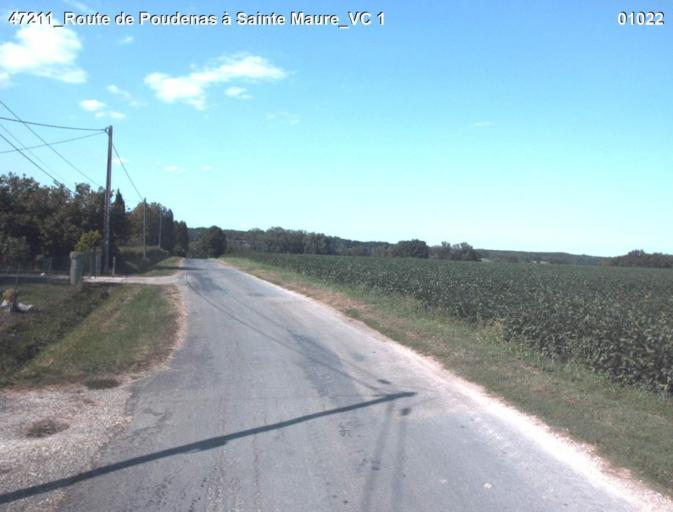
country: FR
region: Aquitaine
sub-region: Departement du Lot-et-Garonne
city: Mezin
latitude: 44.0388
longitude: 0.2098
